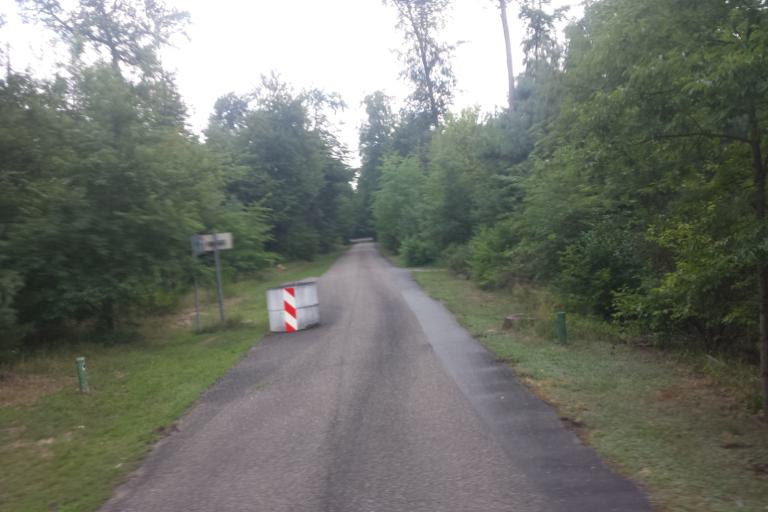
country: DE
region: Hesse
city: Lorsch
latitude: 49.5994
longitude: 8.5378
